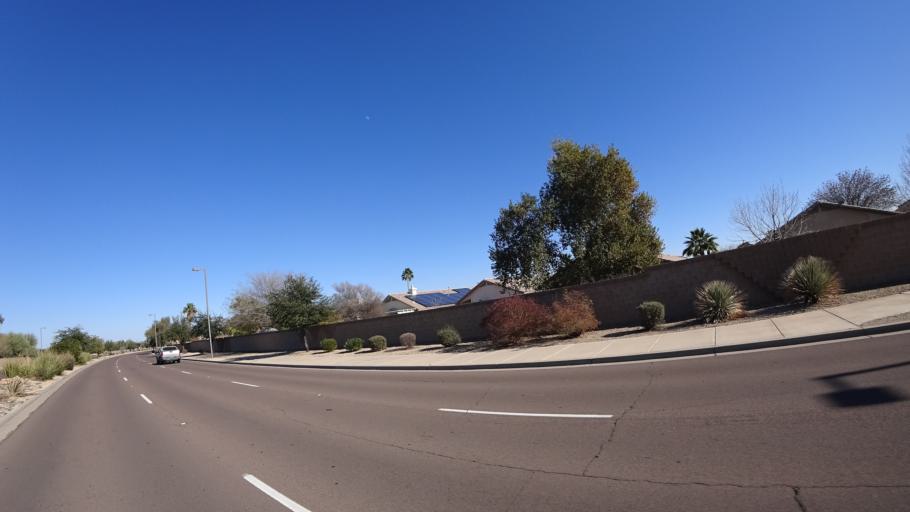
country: US
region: Arizona
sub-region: Maricopa County
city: Sun City West
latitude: 33.6463
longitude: -112.3896
